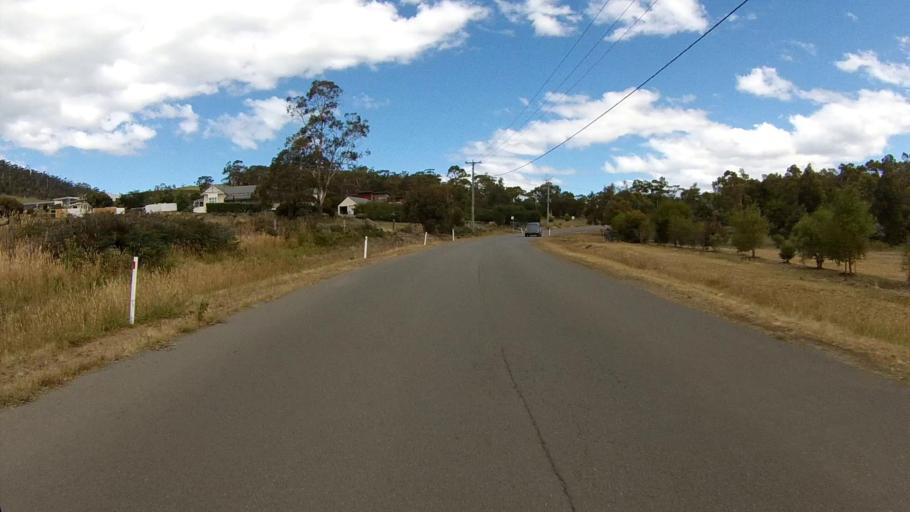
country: AU
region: Tasmania
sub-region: Clarence
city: Acton Park
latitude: -42.8706
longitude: 147.4908
